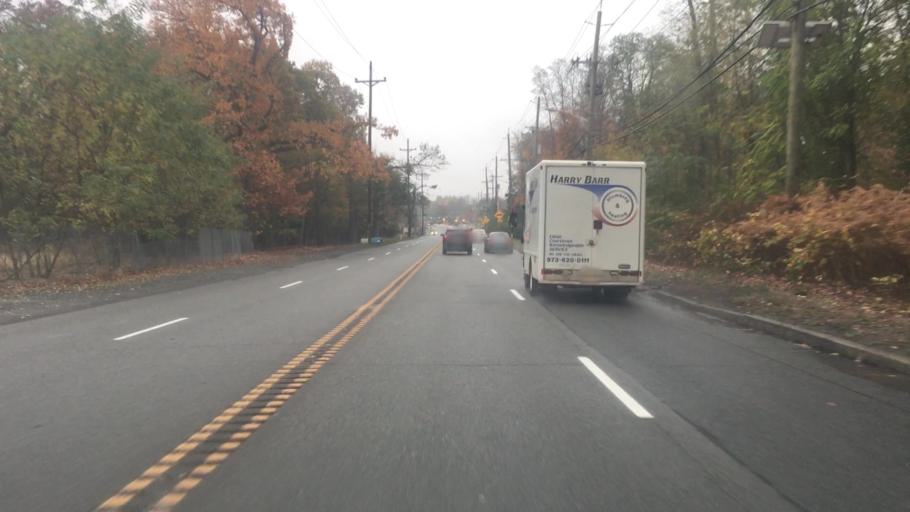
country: US
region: New Jersey
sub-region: Passaic County
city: Wayne
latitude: 40.9670
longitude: -74.2573
